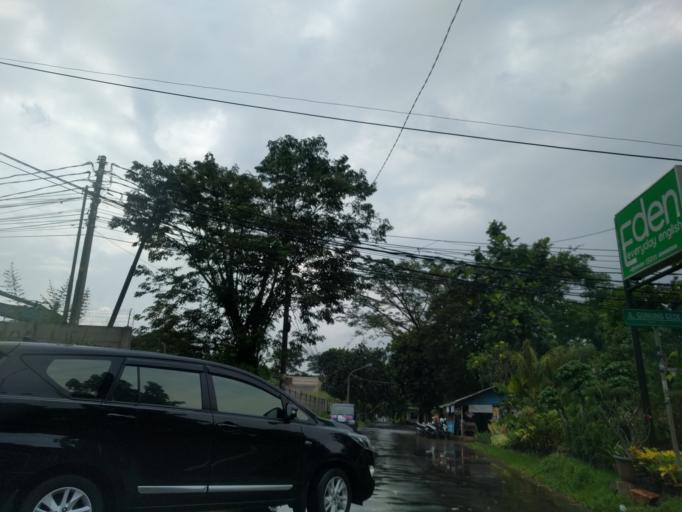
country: ID
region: West Java
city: Bogor
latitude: -6.5846
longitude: 106.8060
